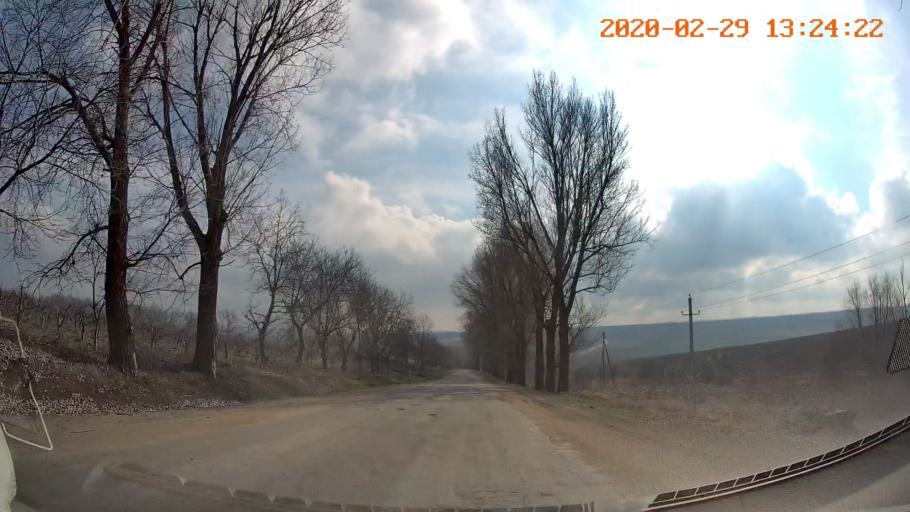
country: MD
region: Telenesti
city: Camenca
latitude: 47.9396
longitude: 28.6271
